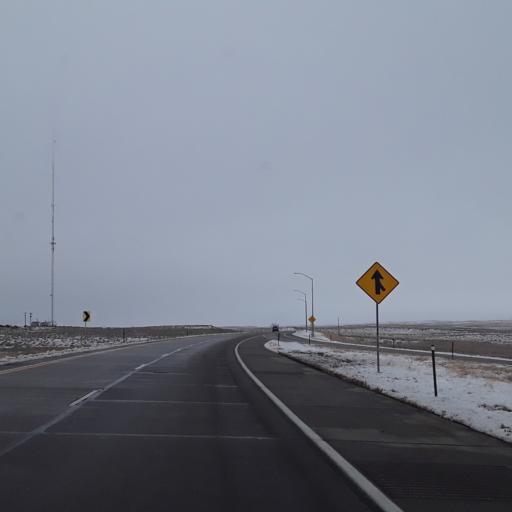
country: US
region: Colorado
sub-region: Logan County
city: Sterling
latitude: 40.6247
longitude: -103.1699
